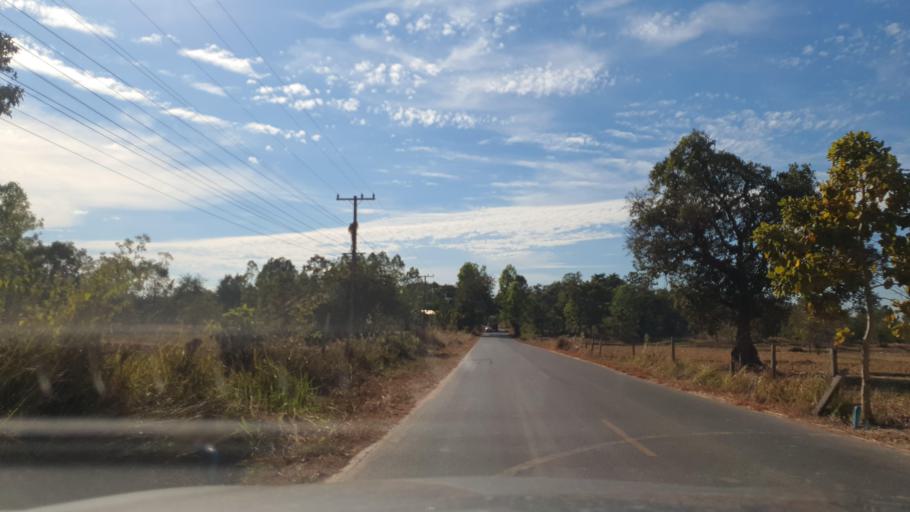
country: TH
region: Kalasin
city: Kuchinarai
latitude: 16.5415
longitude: 104.0852
